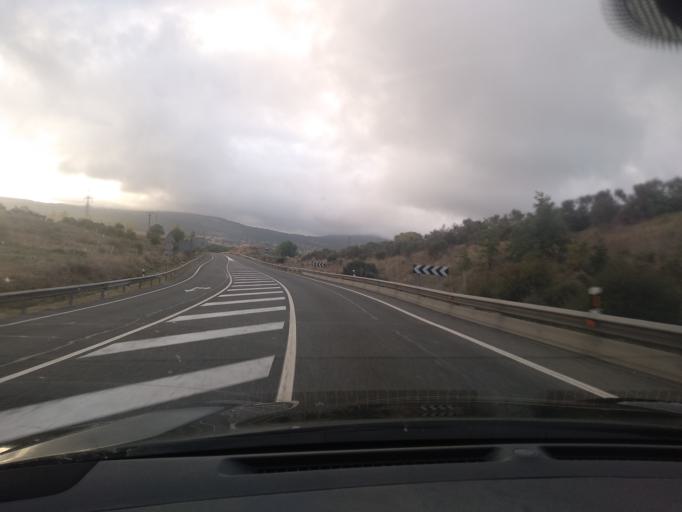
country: ES
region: Castille and Leon
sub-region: Provincia de Segovia
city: Otero de Herreros
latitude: 40.7571
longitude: -4.2102
